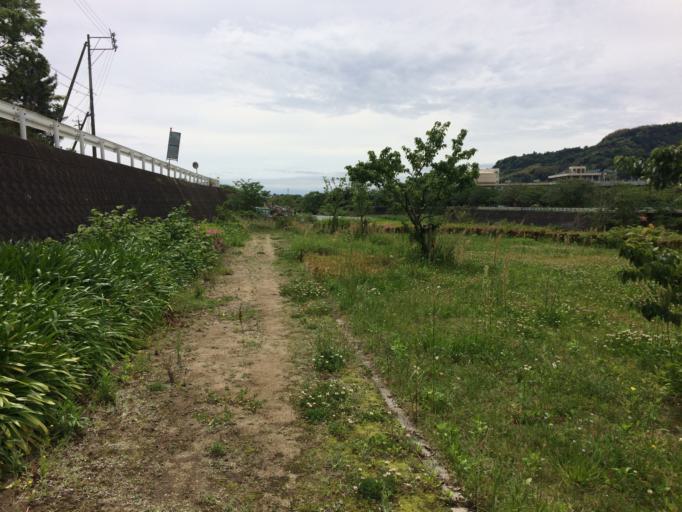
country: JP
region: Shizuoka
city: Fujinomiya
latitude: 35.0740
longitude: 138.5248
